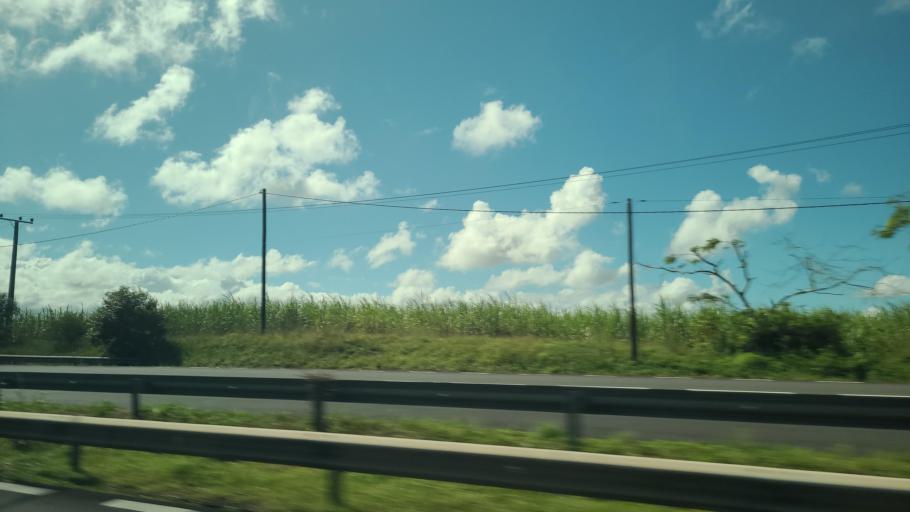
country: MU
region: Grand Port
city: New Grove
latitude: -20.4291
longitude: 57.6247
